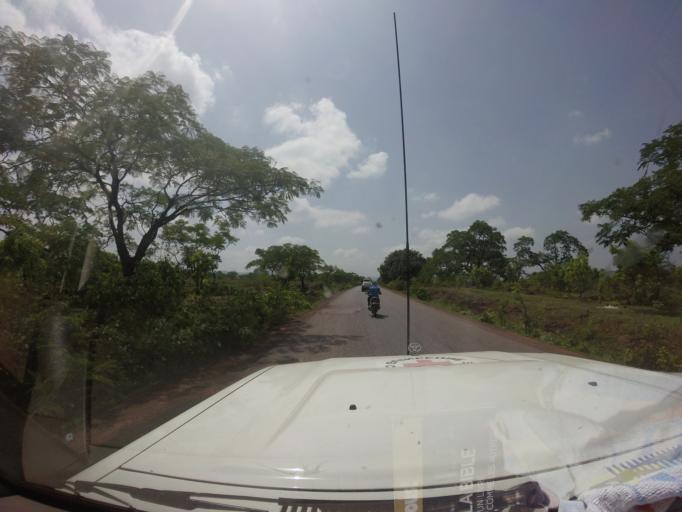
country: GN
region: Mamou
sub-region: Mamou Prefecture
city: Mamou
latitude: 10.2958
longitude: -12.3523
